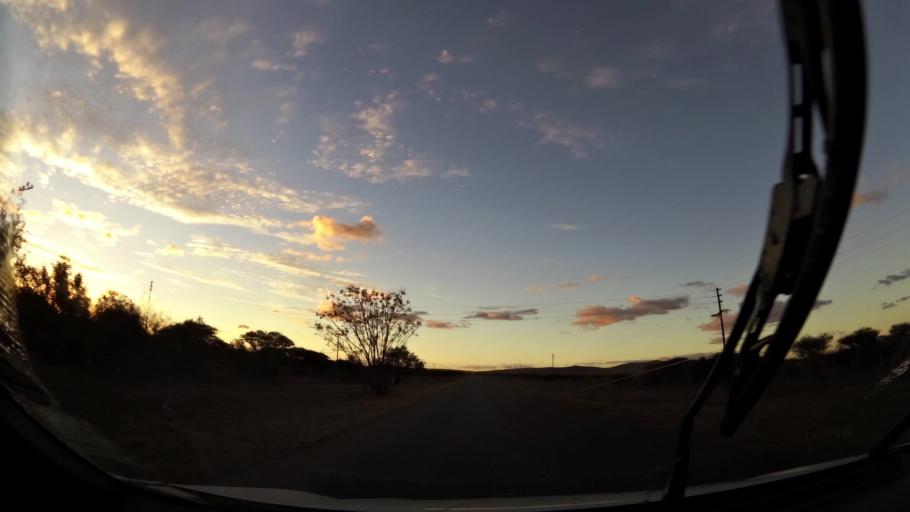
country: ZA
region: Limpopo
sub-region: Capricorn District Municipality
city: Polokwane
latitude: -23.7489
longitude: 29.4715
